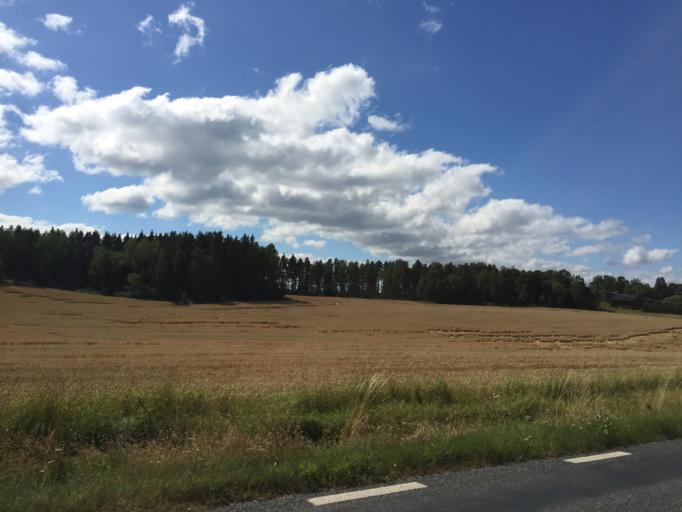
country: SE
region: Soedermanland
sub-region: Nykopings Kommun
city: Olstorp
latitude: 58.8279
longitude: 16.5233
